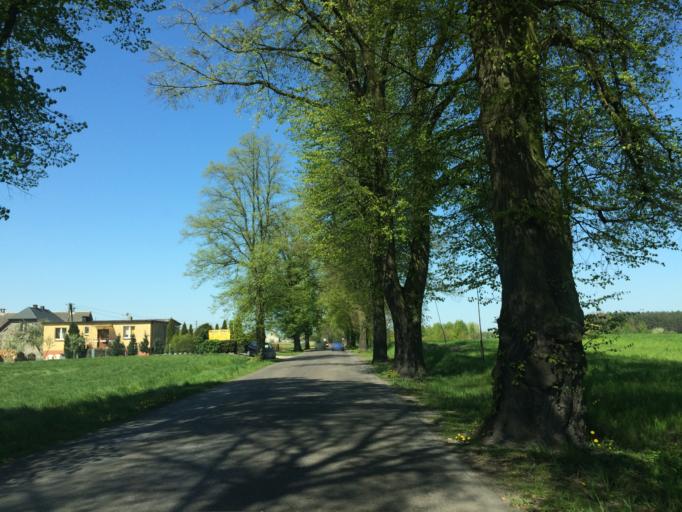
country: PL
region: Warmian-Masurian Voivodeship
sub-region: Powiat nowomiejski
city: Biskupiec
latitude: 53.4945
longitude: 19.3870
